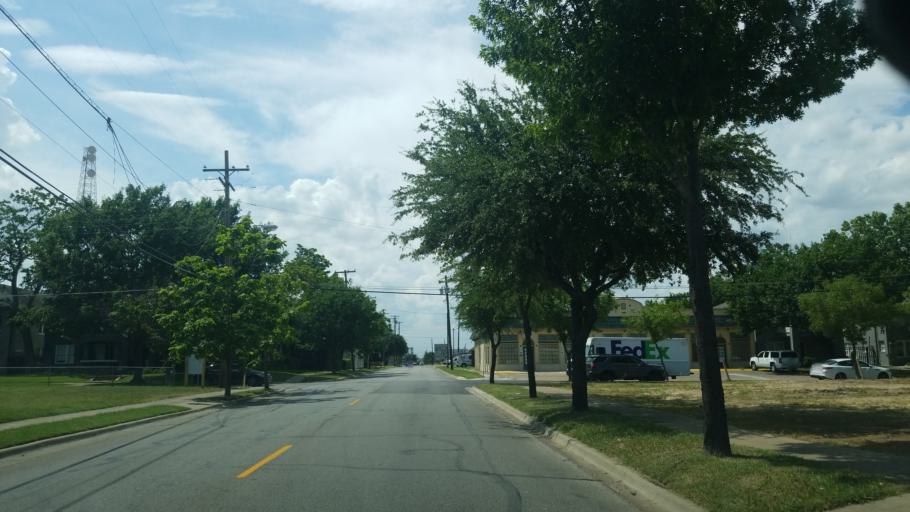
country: US
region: Texas
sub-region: Dallas County
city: Dallas
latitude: 32.7975
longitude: -96.7744
